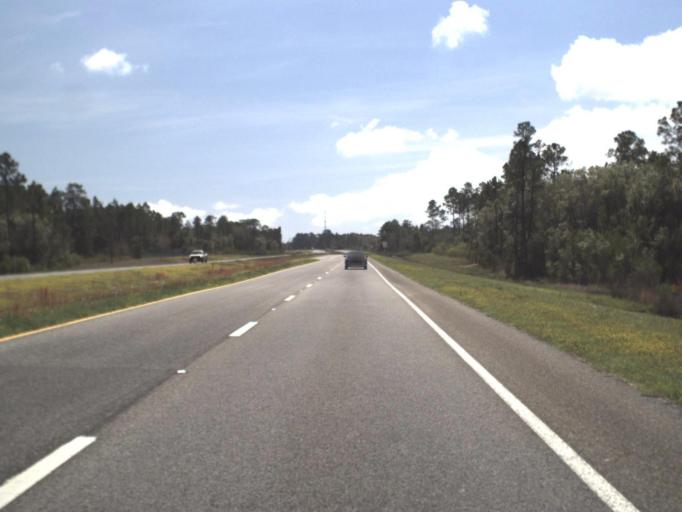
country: US
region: Florida
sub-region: Bay County
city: Laguna Beach
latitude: 30.3436
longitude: -85.8590
